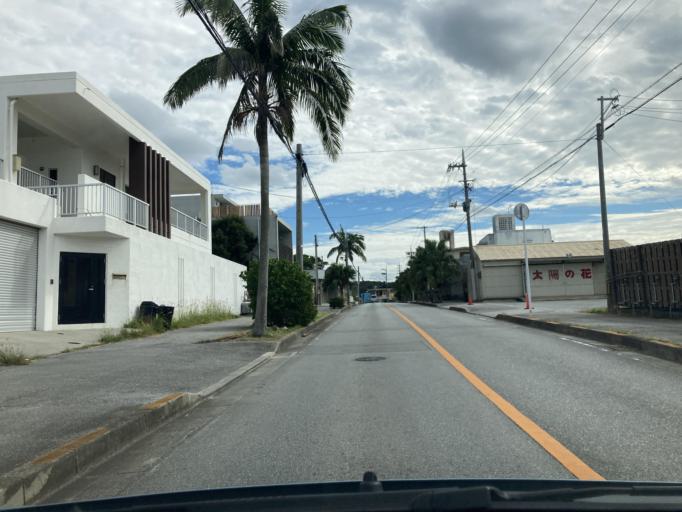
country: JP
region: Okinawa
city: Ishikawa
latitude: 26.4387
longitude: 127.7736
